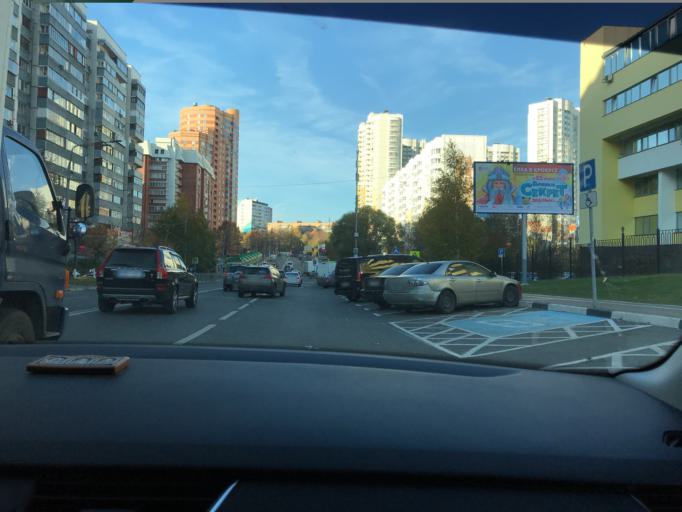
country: RU
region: Moscow
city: Khimki
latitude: 55.8837
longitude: 37.4284
